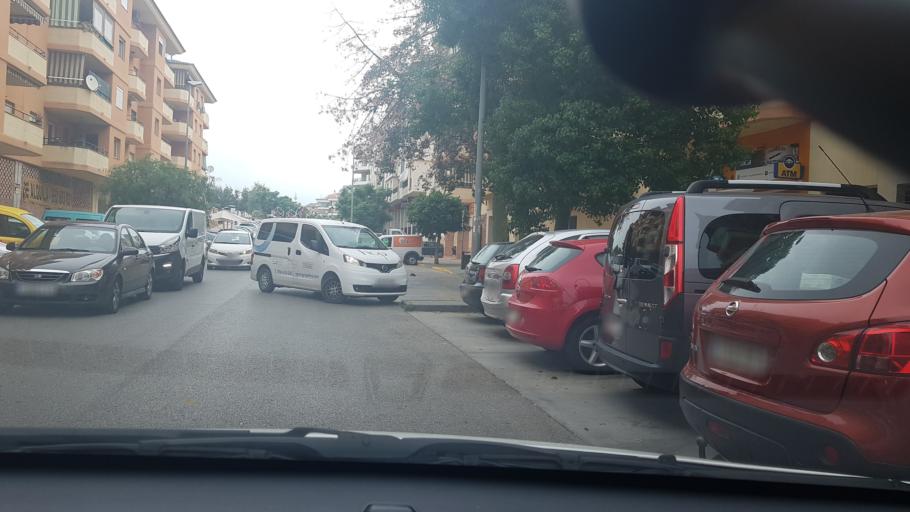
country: ES
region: Andalusia
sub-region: Provincia de Malaga
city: Manilva
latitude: 36.3644
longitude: -5.2302
